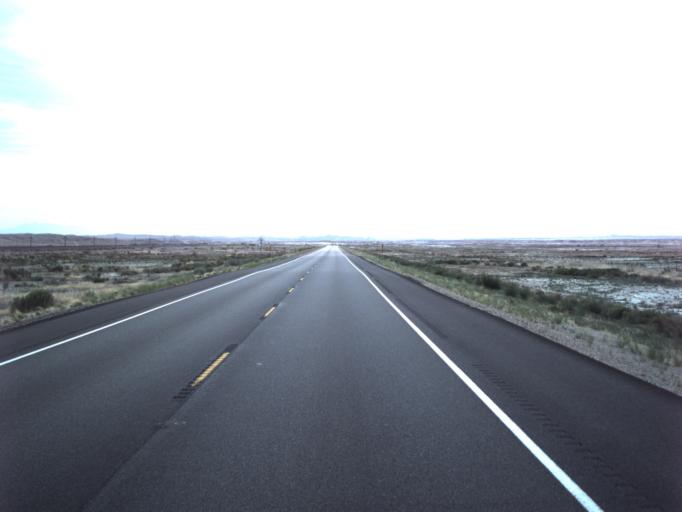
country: US
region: Utah
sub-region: Carbon County
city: East Carbon City
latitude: 39.0115
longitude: -110.2833
